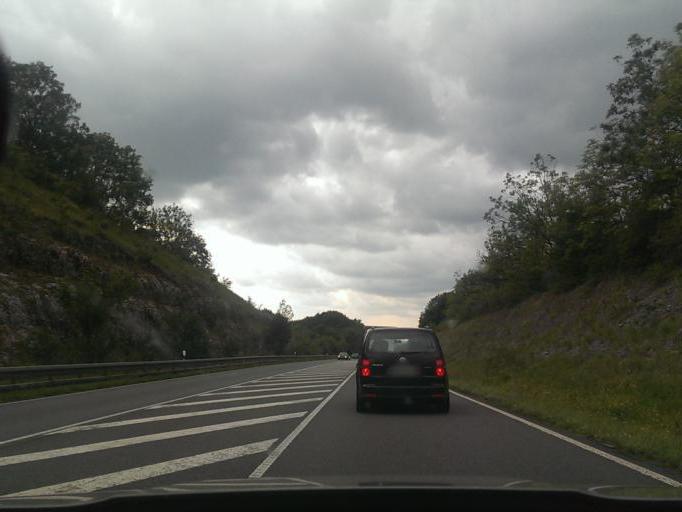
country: DE
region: North Rhine-Westphalia
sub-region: Regierungsbezirk Detmold
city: Schlangen
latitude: 51.8263
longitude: 8.8731
